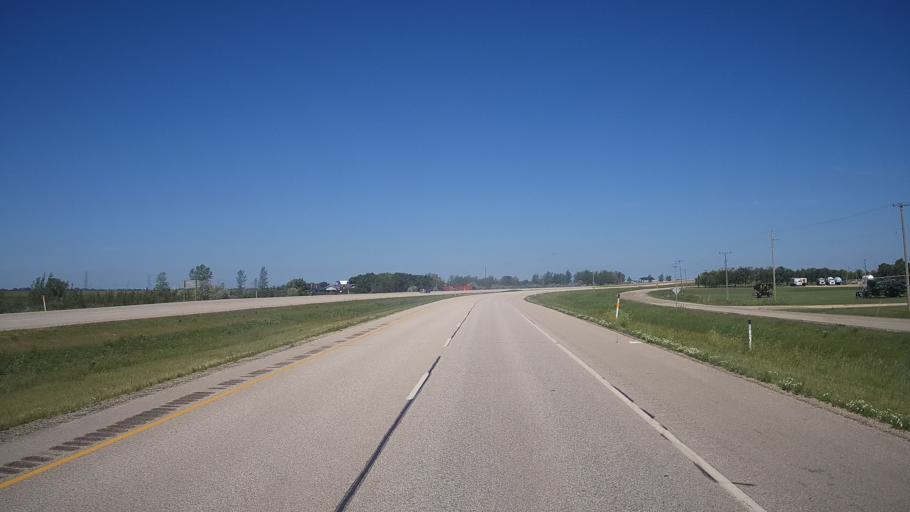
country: CA
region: Manitoba
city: Portage la Prairie
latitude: 49.9614
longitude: -98.3487
